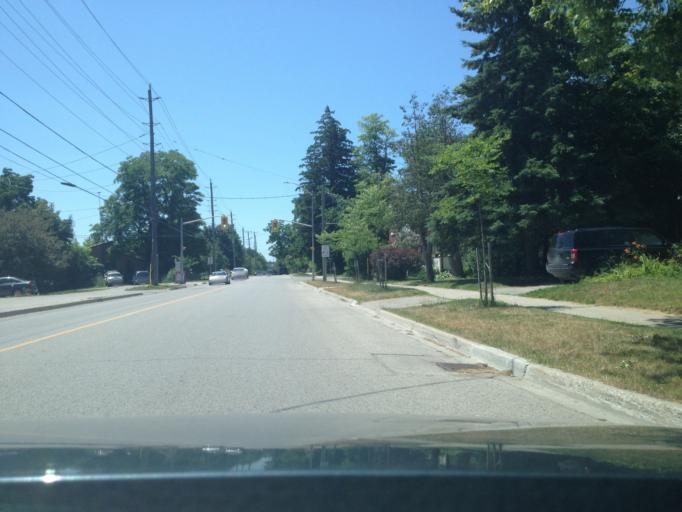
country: CA
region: Ontario
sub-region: Wellington County
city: Guelph
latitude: 43.6850
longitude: -80.4230
